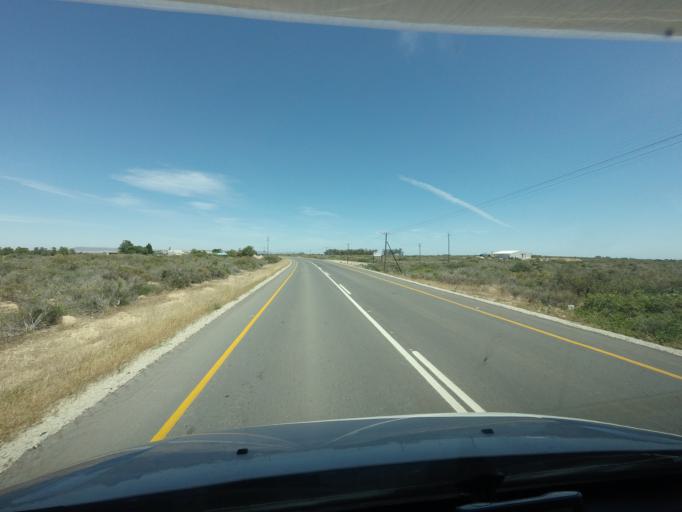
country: ZA
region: Western Cape
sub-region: West Coast District Municipality
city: Vredenburg
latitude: -32.7911
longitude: 18.2206
